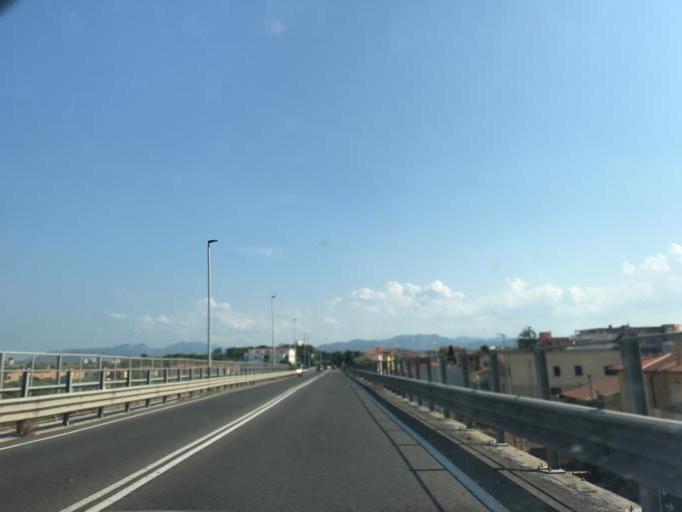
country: IT
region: Sardinia
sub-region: Provincia di Olbia-Tempio
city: Olbia
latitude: 40.9176
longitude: 9.5015
